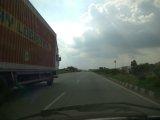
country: IN
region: Karnataka
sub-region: Kolar
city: Kolar
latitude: 13.1349
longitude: 78.0171
